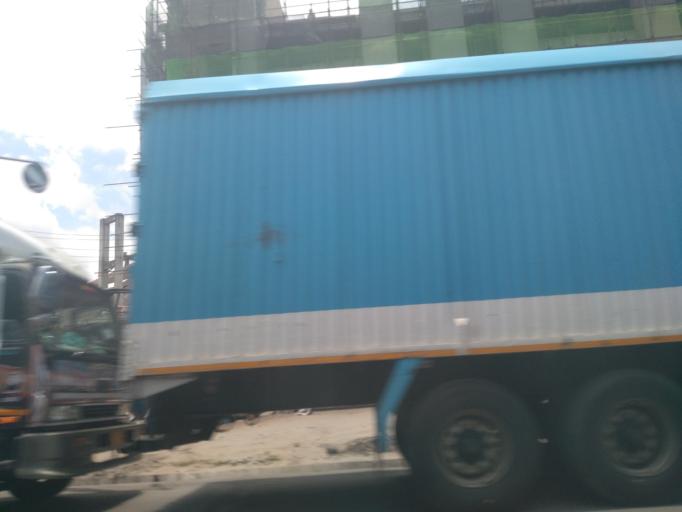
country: TZ
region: Dar es Salaam
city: Dar es Salaam
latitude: -6.8316
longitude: 39.2880
